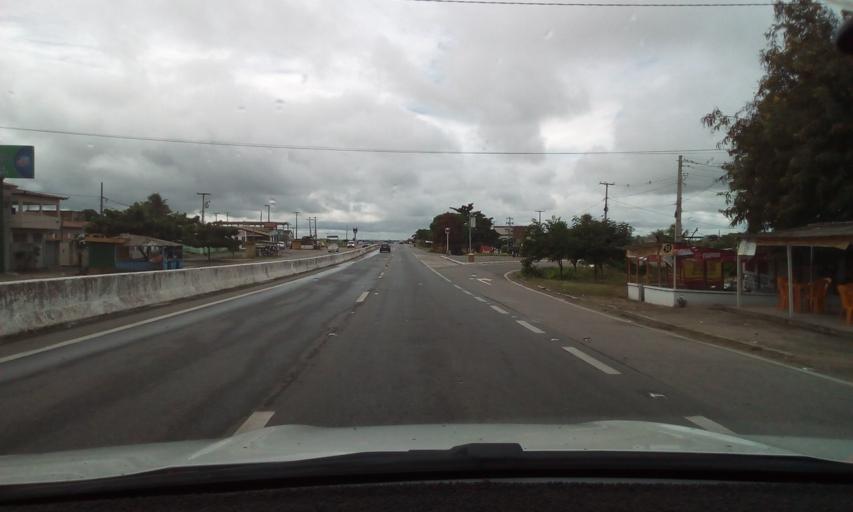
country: BR
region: Paraiba
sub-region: Gurinhem
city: Gurinhem
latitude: -7.1730
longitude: -35.3931
